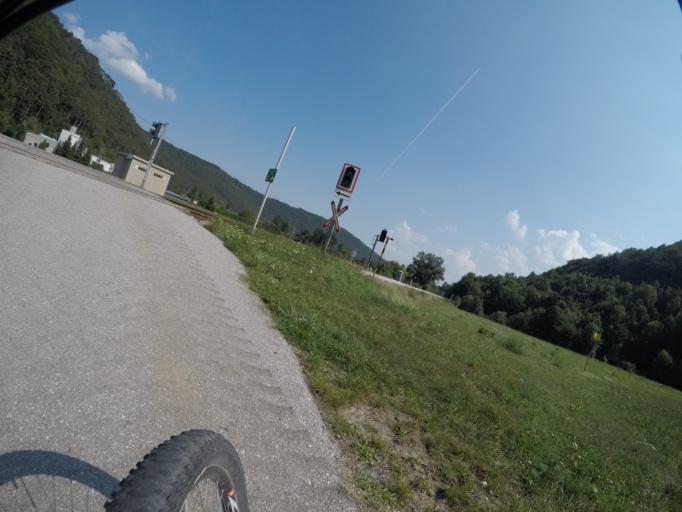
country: AT
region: Lower Austria
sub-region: Politischer Bezirk Baden
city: Weissenbach an der Triesting
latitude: 47.9833
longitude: 16.0531
